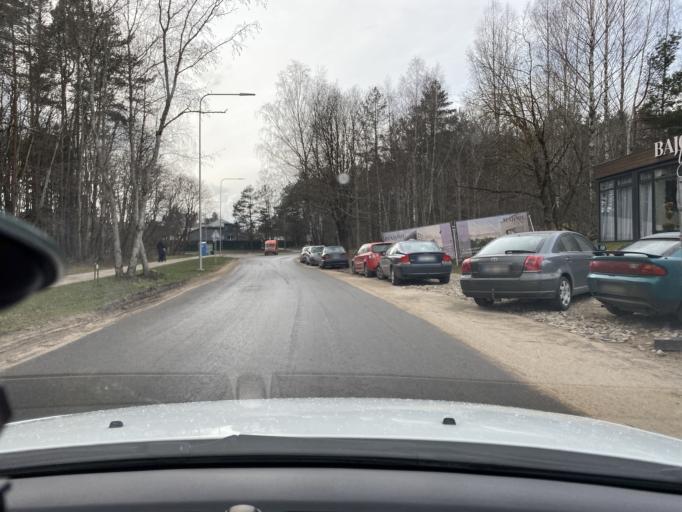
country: LT
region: Vilnius County
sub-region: Vilnius
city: Fabijoniskes
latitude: 54.7573
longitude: 25.2581
